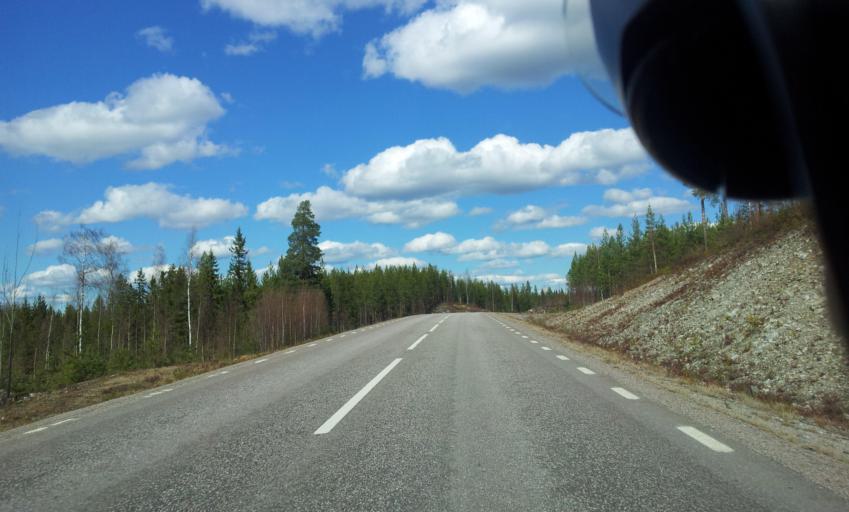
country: SE
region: Gaevleborg
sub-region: Ovanakers Kommun
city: Edsbyn
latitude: 61.2438
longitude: 15.8838
